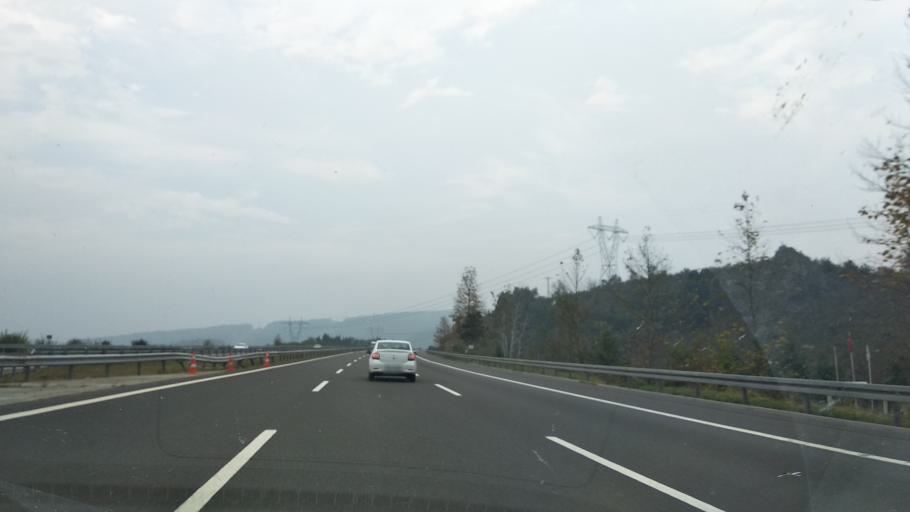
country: TR
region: Duzce
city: Kaynasli
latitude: 40.7862
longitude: 31.2973
